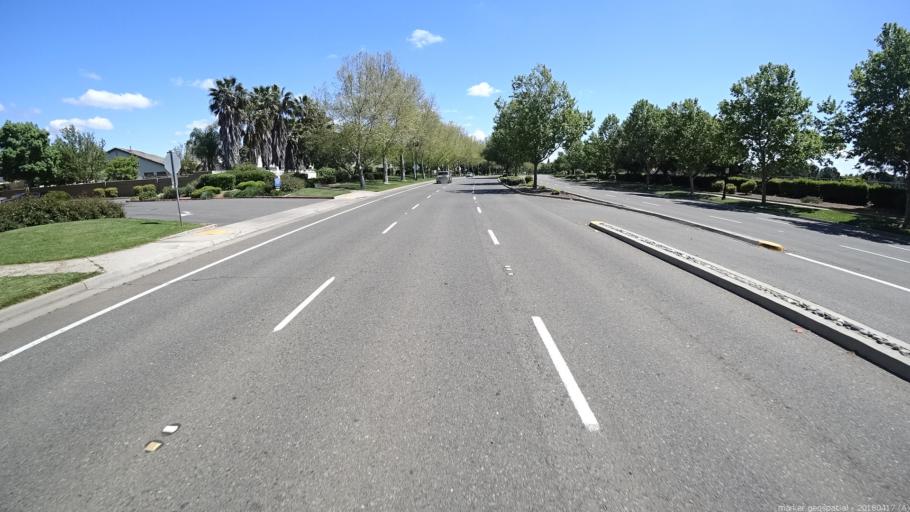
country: US
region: California
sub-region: Sacramento County
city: Laguna
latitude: 38.4077
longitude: -121.4753
